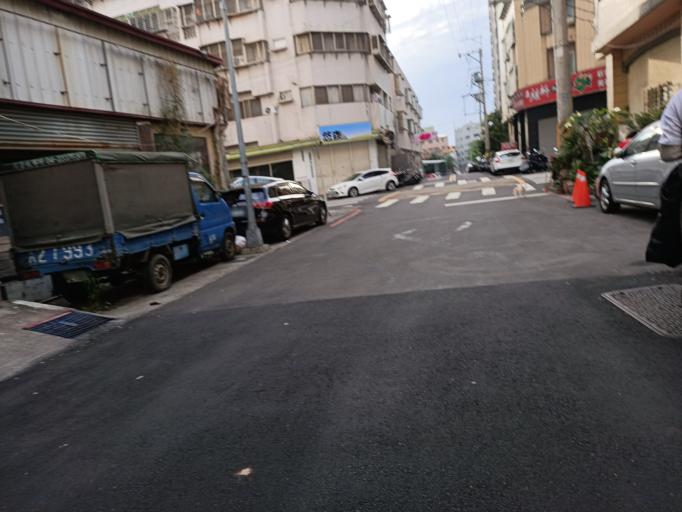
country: TW
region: Taiwan
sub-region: Taichung City
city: Taichung
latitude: 24.1391
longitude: 120.6106
